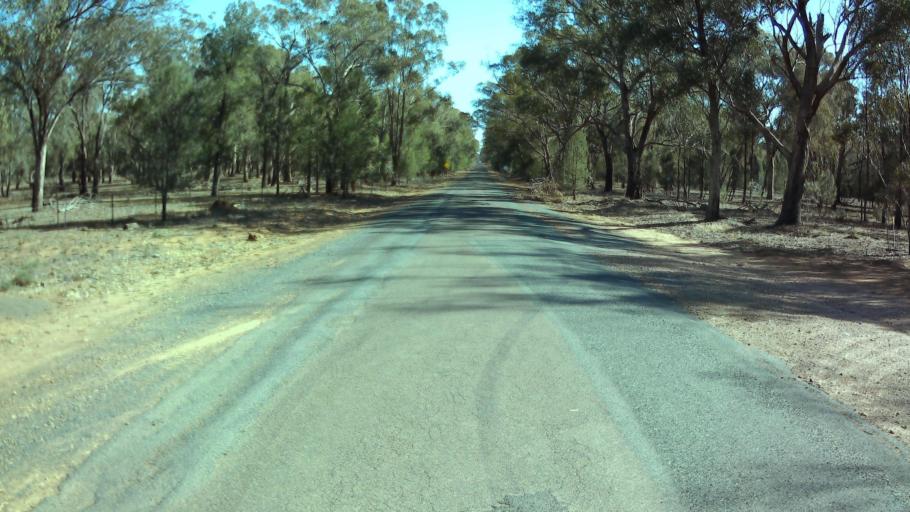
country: AU
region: New South Wales
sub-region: Weddin
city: Grenfell
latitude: -33.8150
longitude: 147.9533
